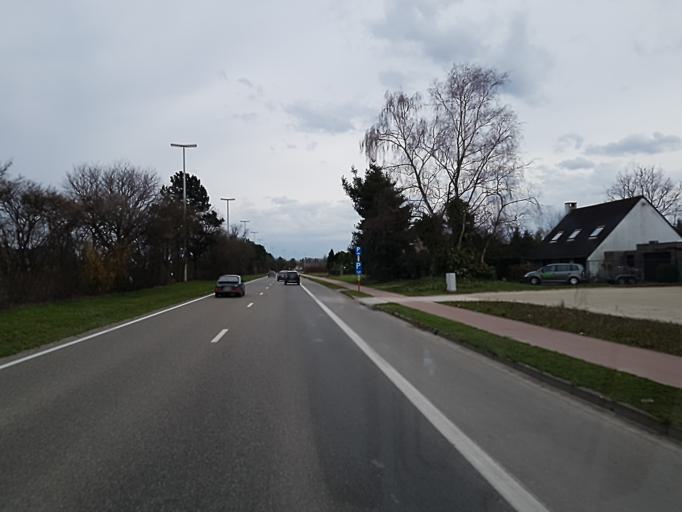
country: BE
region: Flanders
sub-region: Provincie Antwerpen
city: Turnhout
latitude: 51.3306
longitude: 4.9630
